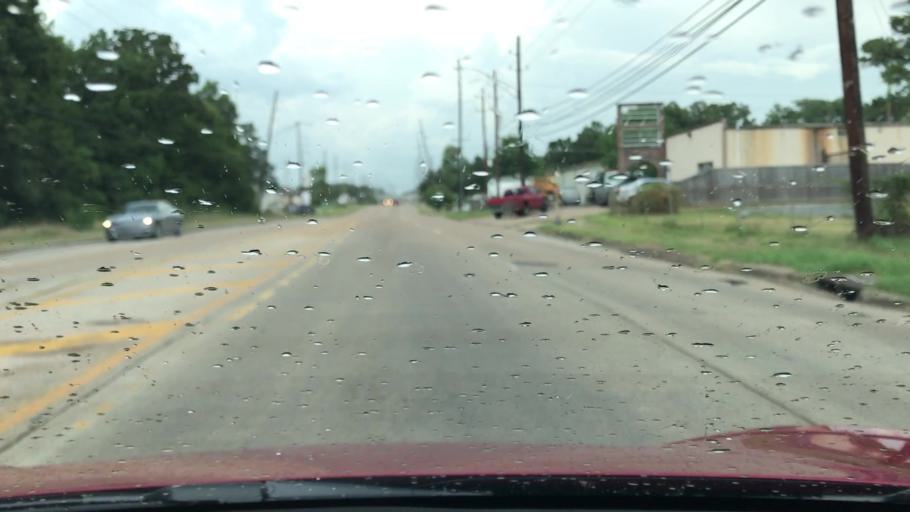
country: US
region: Louisiana
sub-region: Bossier Parish
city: Bossier City
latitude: 32.4136
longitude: -93.7631
